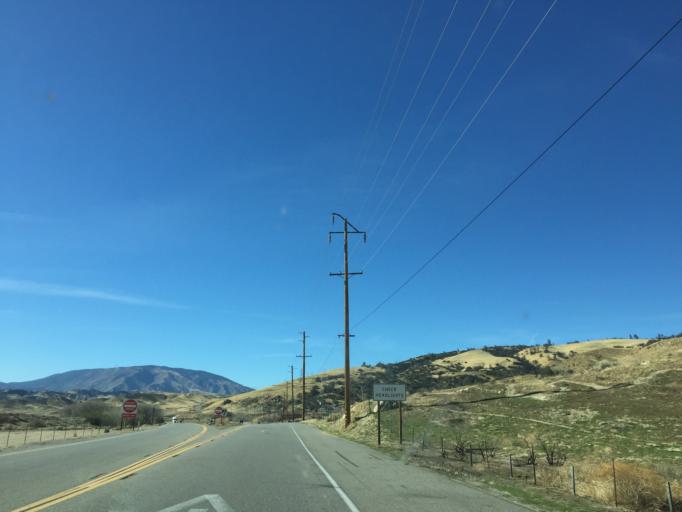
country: US
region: California
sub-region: Kern County
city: Lebec
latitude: 34.7737
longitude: -118.7656
